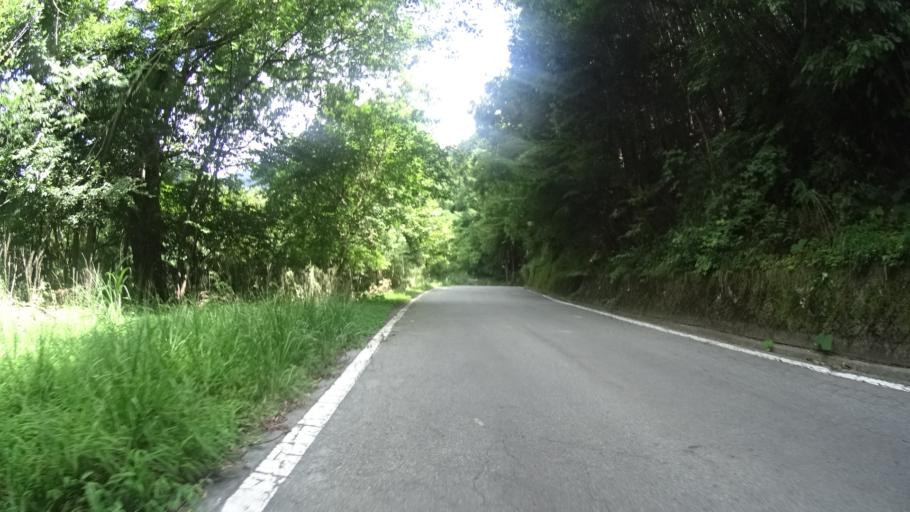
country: JP
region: Yamanashi
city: Enzan
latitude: 35.7849
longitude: 138.6938
